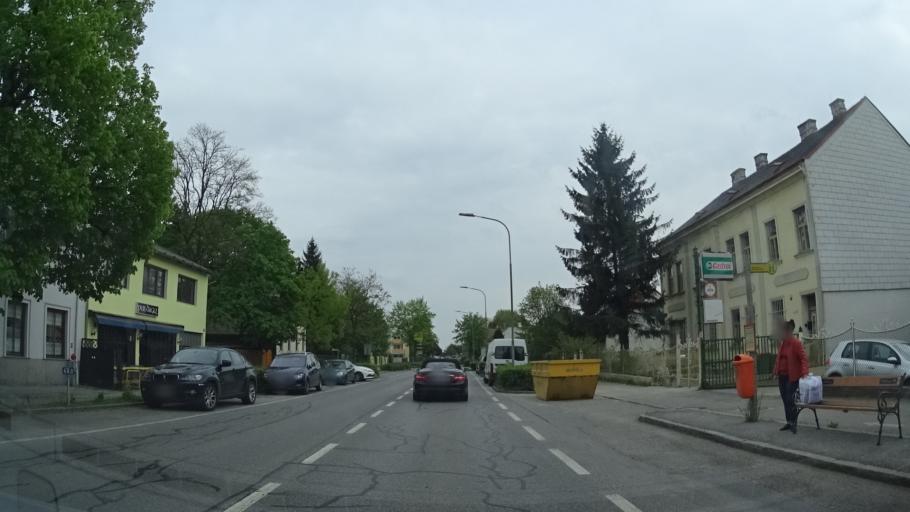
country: AT
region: Lower Austria
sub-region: Politischer Bezirk Korneuburg
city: Langenzersdorf
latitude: 48.3068
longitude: 16.3624
